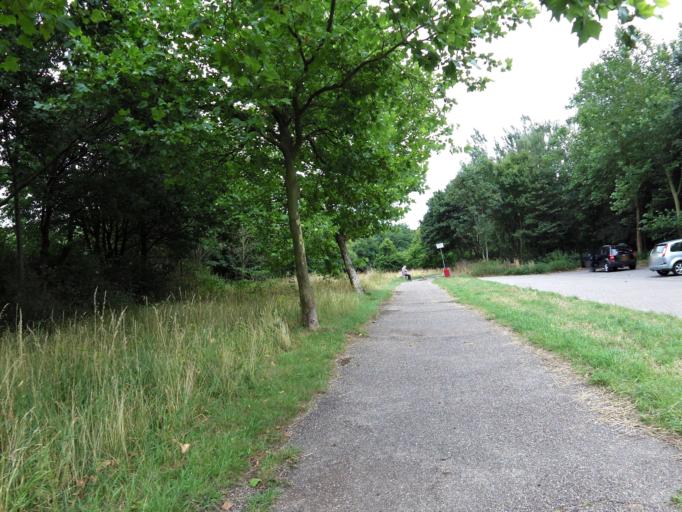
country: NL
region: Limburg
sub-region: Gemeente Brunssum
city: Brunssum
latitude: 50.9325
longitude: 5.9526
